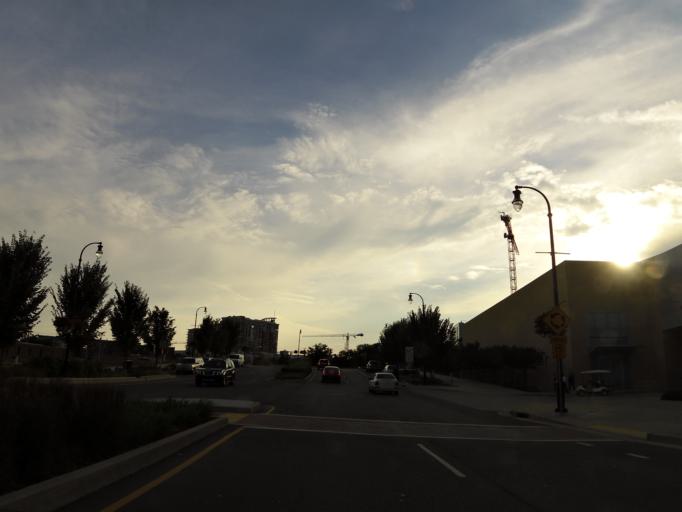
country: US
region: Tennessee
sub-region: Davidson County
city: Nashville
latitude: 36.1555
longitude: -86.7781
